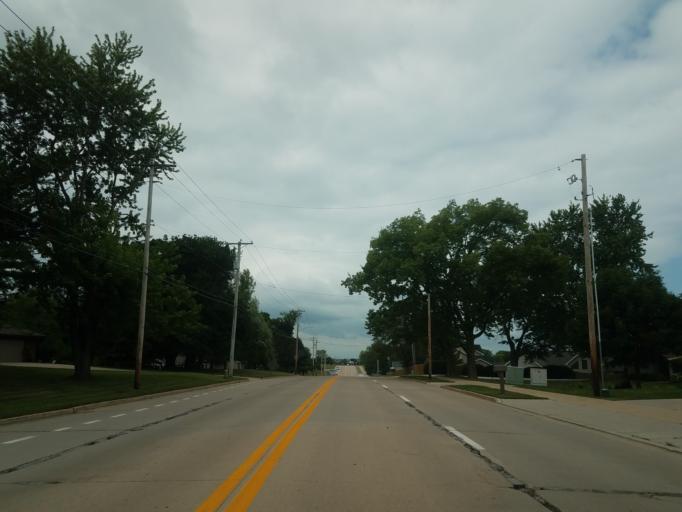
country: US
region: Illinois
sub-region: McLean County
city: Bloomington
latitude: 40.4513
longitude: -89.0311
